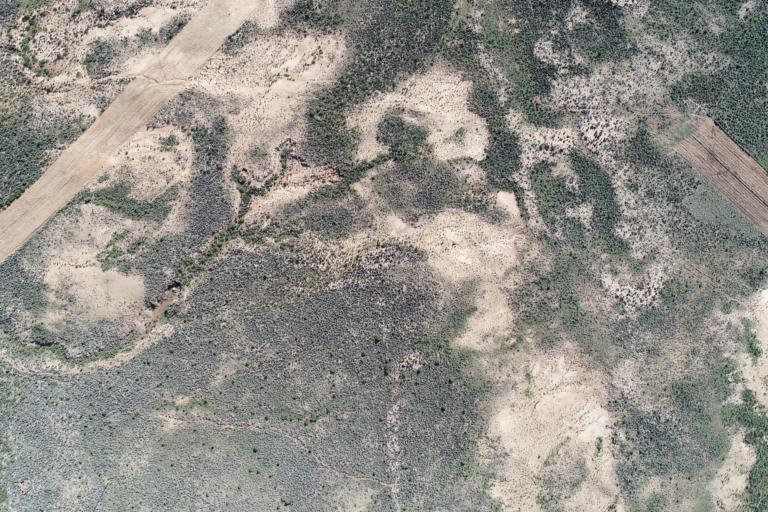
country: BO
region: La Paz
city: Curahuara de Carangas
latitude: -17.3028
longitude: -68.5185
